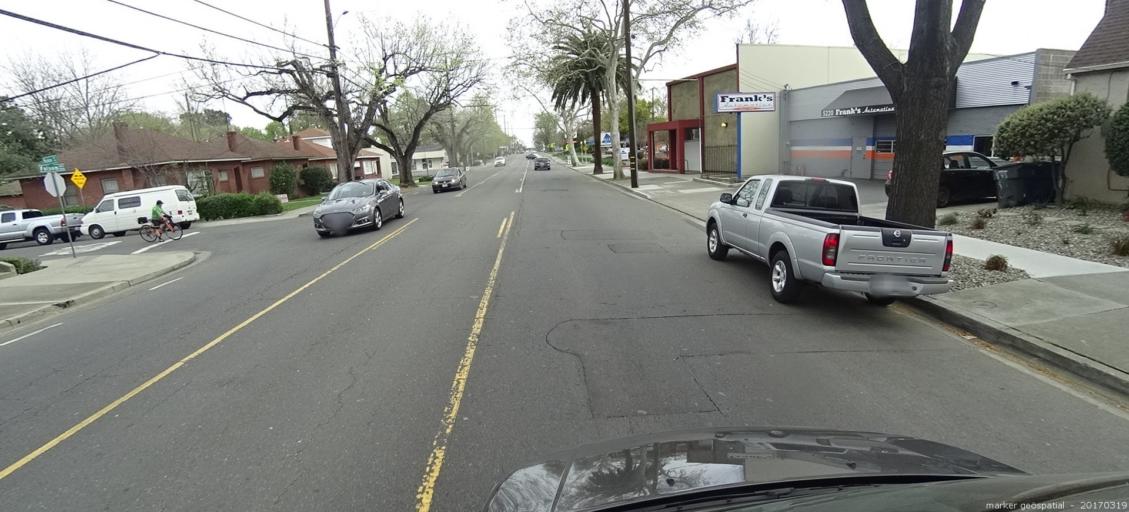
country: US
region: California
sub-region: Sacramento County
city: Sacramento
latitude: 38.5602
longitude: -121.4427
